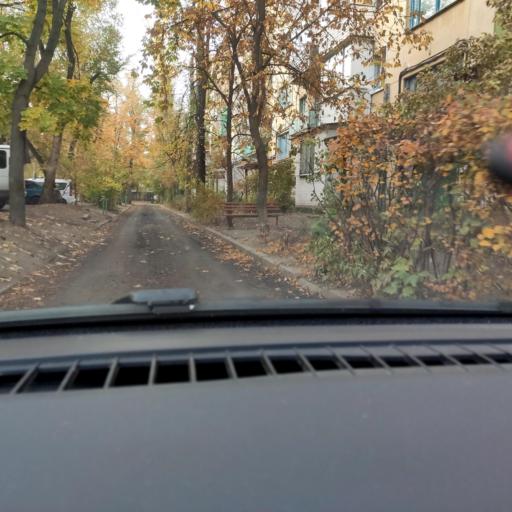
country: RU
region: Voronezj
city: Voronezh
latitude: 51.6959
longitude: 39.2676
